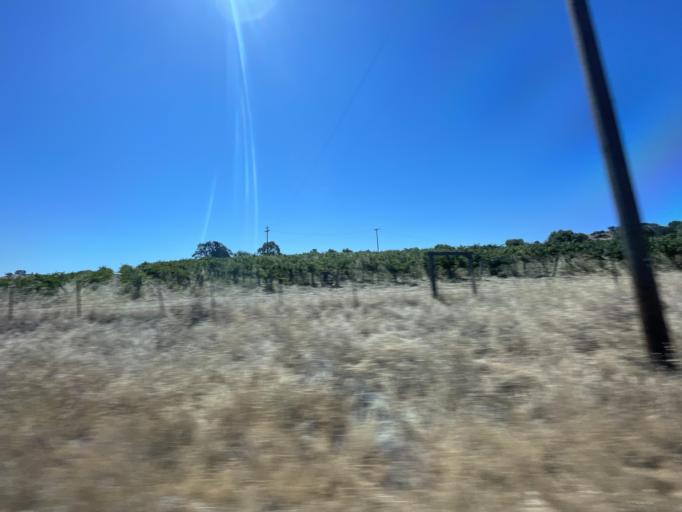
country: US
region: California
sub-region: San Luis Obispo County
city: Paso Robles
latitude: 35.6321
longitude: -120.6020
